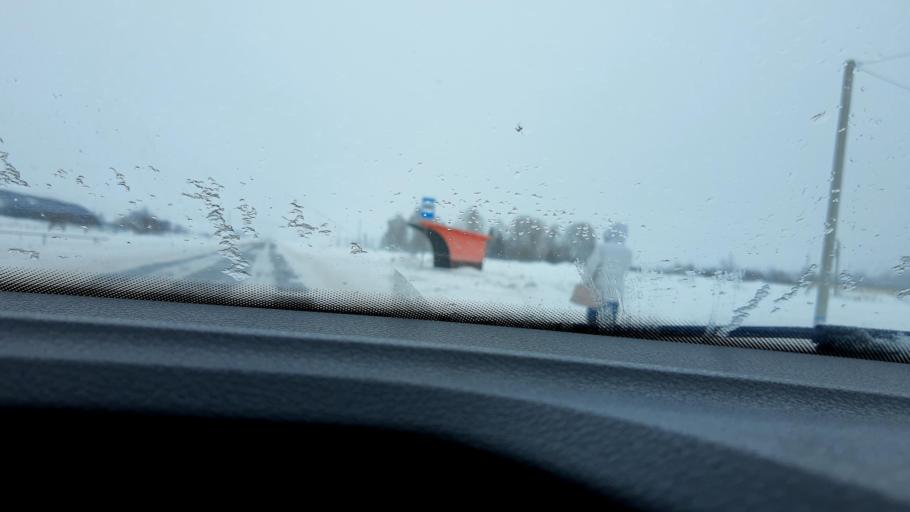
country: RU
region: Bashkortostan
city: Zirgan
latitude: 53.2321
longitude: 55.9160
